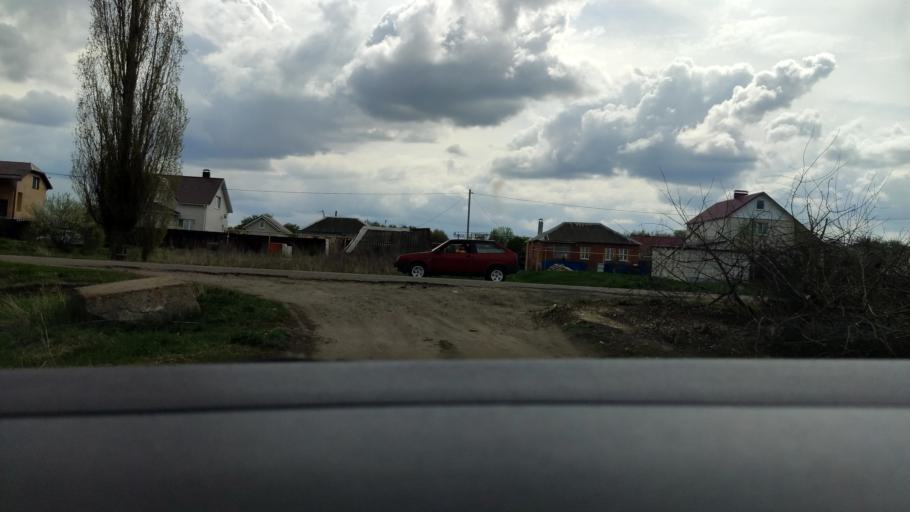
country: RU
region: Voronezj
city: Semiluki
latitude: 51.7798
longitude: 39.0003
